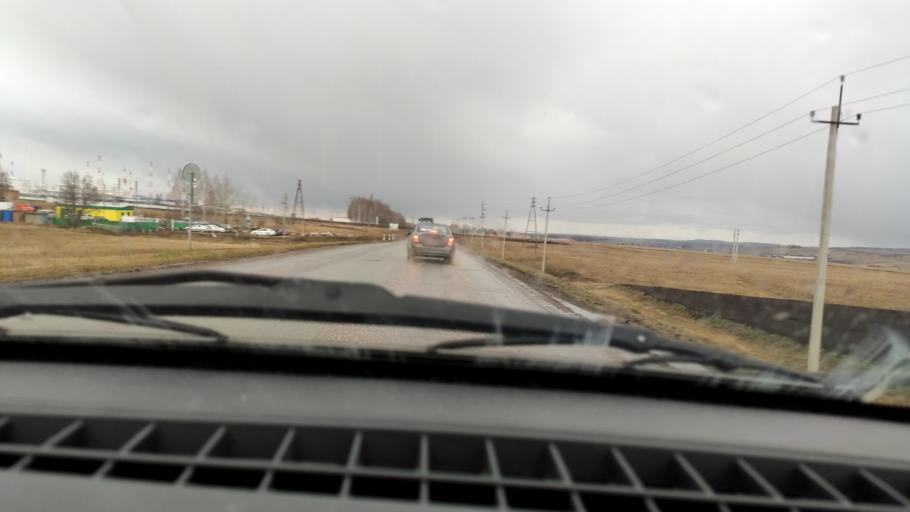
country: RU
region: Bashkortostan
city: Chekmagush
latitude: 55.1145
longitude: 54.8658
